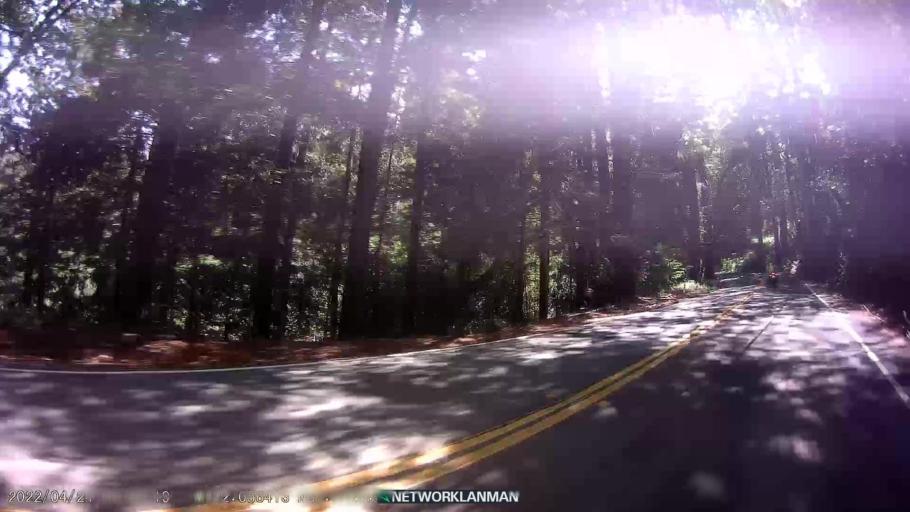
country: US
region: California
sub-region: Santa Cruz County
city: Lompico
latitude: 37.1719
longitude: -122.0564
